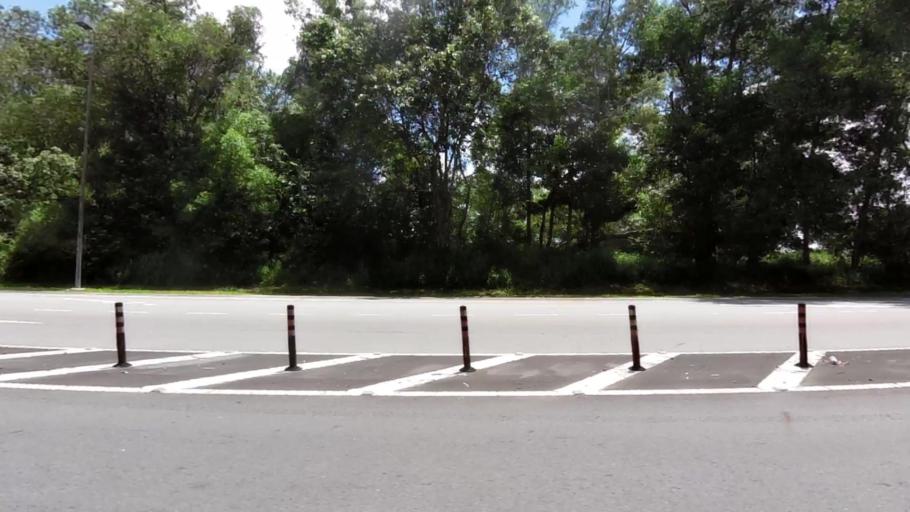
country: BN
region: Brunei and Muara
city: Bandar Seri Begawan
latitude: 4.9273
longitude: 114.9577
